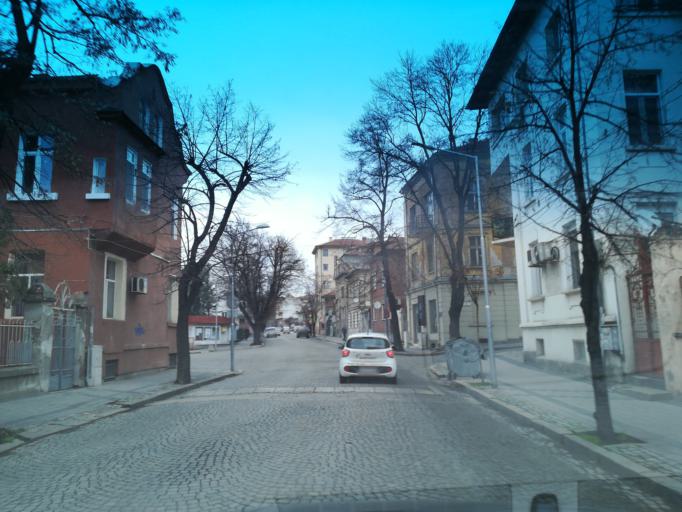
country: BG
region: Plovdiv
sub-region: Obshtina Plovdiv
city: Plovdiv
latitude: 42.1453
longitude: 24.7442
